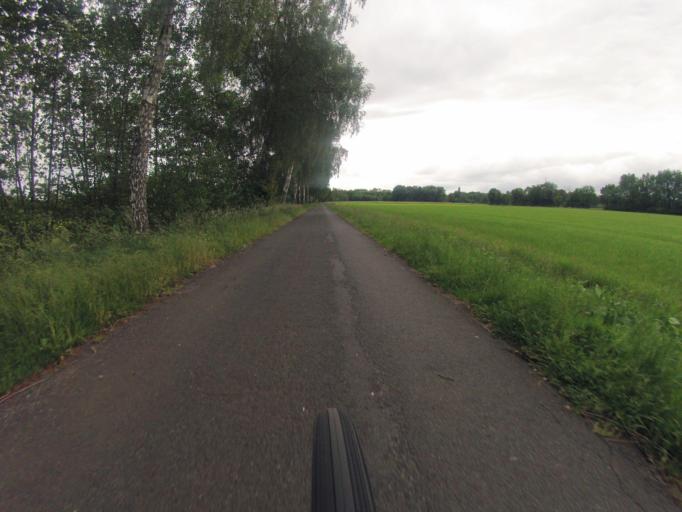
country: DE
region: North Rhine-Westphalia
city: Ibbenburen
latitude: 52.2469
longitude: 7.7566
